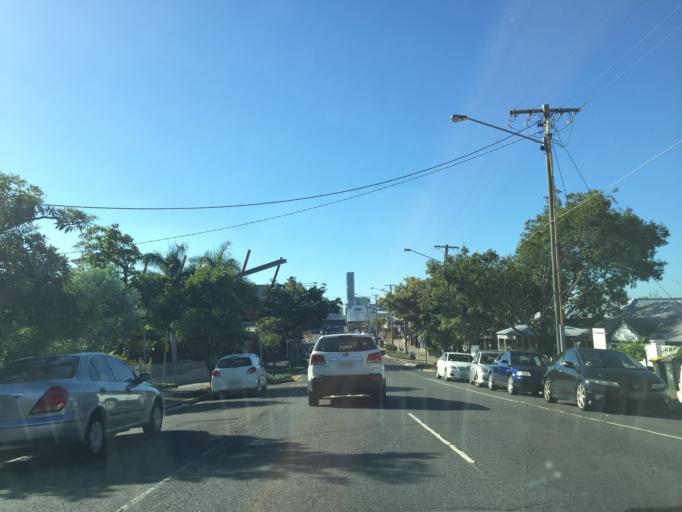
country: AU
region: Queensland
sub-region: Brisbane
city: Milton
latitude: -27.4587
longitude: 152.9969
